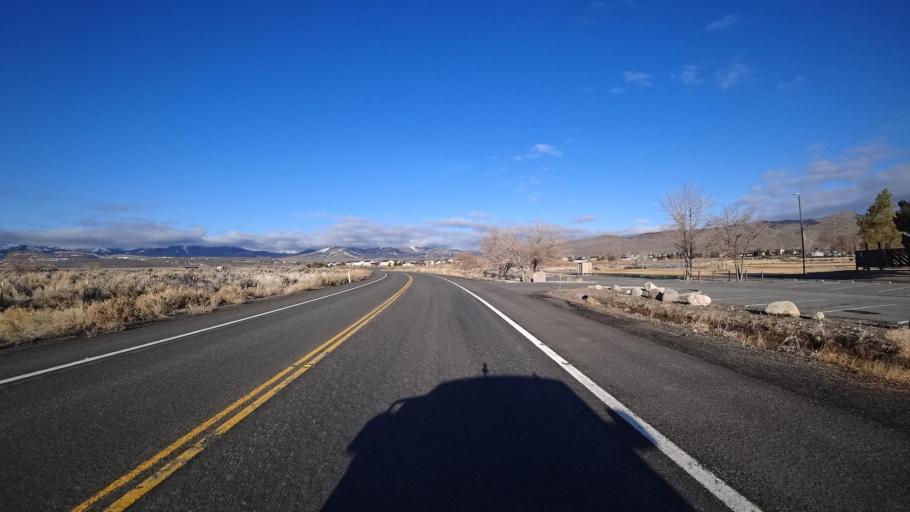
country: US
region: Nevada
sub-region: Washoe County
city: Cold Springs
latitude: 39.6756
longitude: -119.9764
